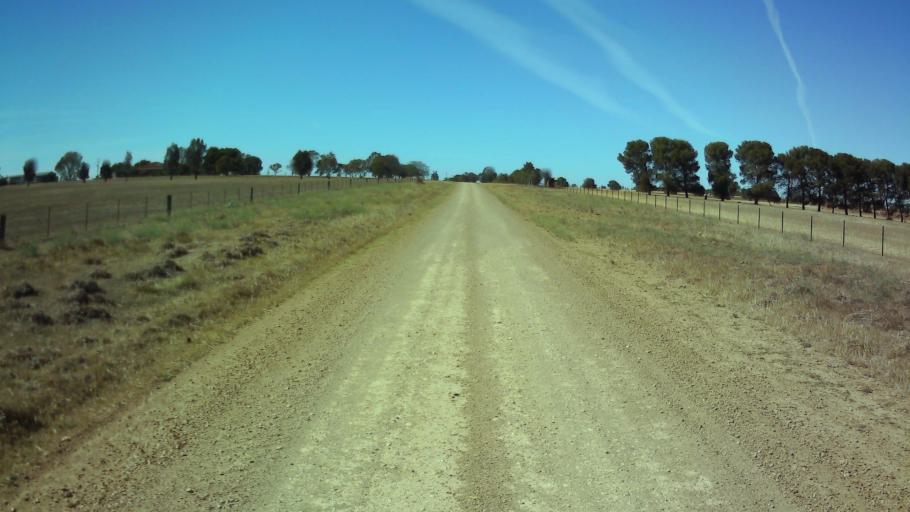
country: AU
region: New South Wales
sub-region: Weddin
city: Grenfell
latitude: -34.0531
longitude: 148.1724
